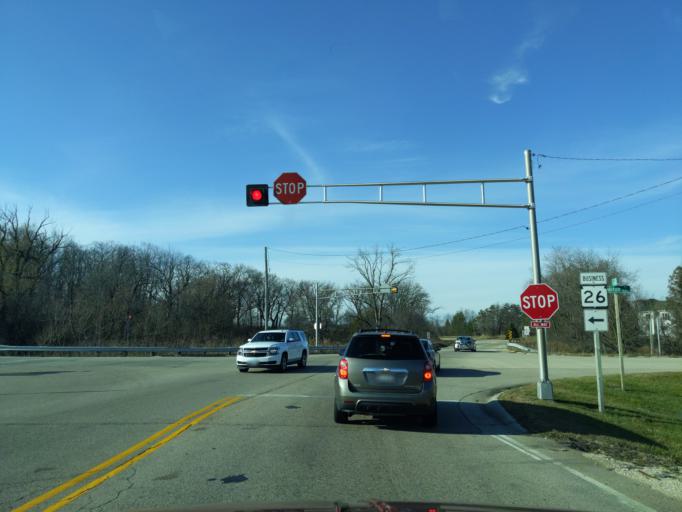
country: US
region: Wisconsin
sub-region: Rock County
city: Milton
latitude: 42.8222
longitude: -88.9317
